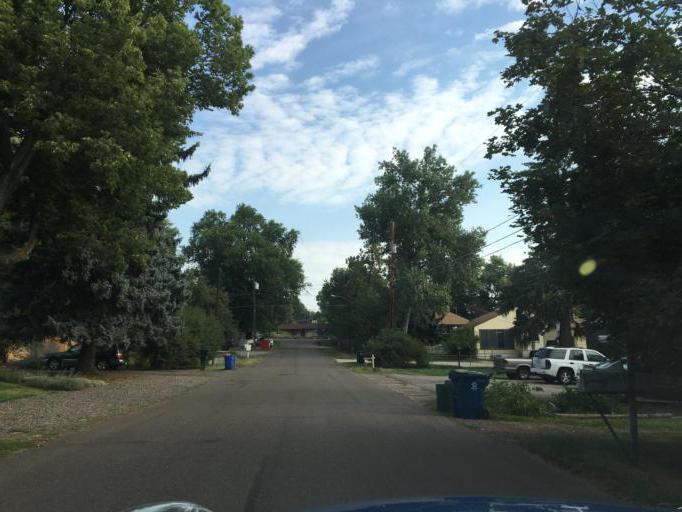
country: US
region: Colorado
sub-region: Jefferson County
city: Wheat Ridge
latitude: 39.7461
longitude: -105.1037
